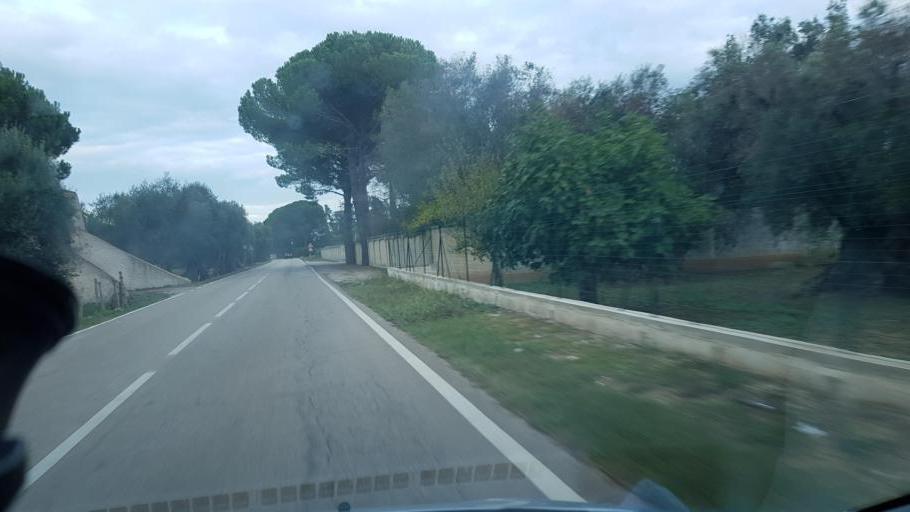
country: IT
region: Apulia
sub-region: Provincia di Brindisi
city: Oria
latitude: 40.5146
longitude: 17.6699
